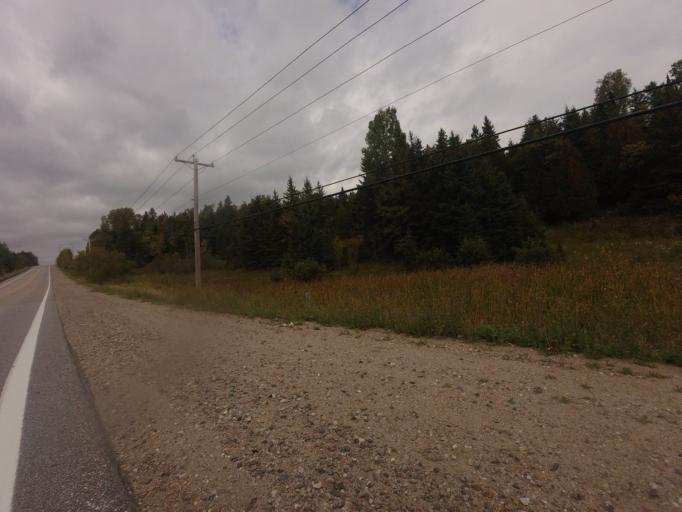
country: CA
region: Quebec
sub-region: Outaouais
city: Wakefield
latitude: 45.9338
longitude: -75.9938
